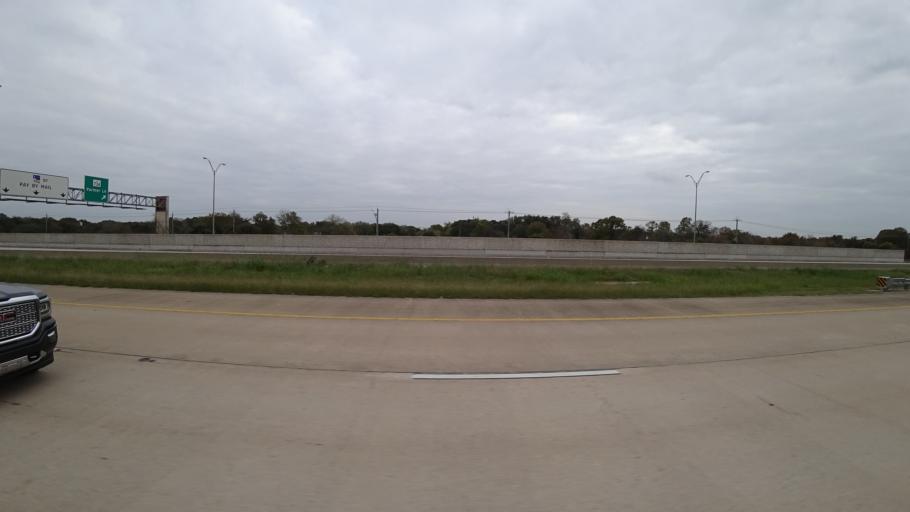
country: US
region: Texas
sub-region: Williamson County
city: Anderson Mill
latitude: 30.4737
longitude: -97.7807
